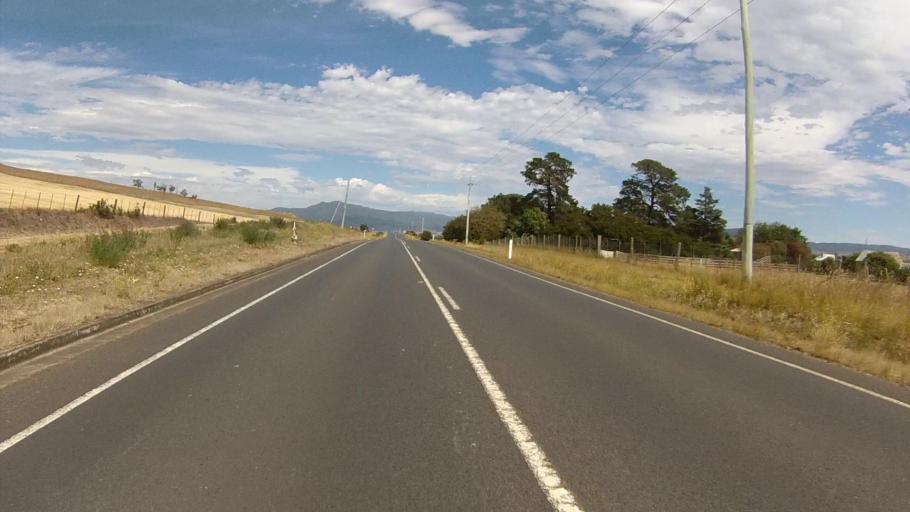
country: AU
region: Tasmania
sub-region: Brighton
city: Bridgewater
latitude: -42.6904
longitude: 147.3068
